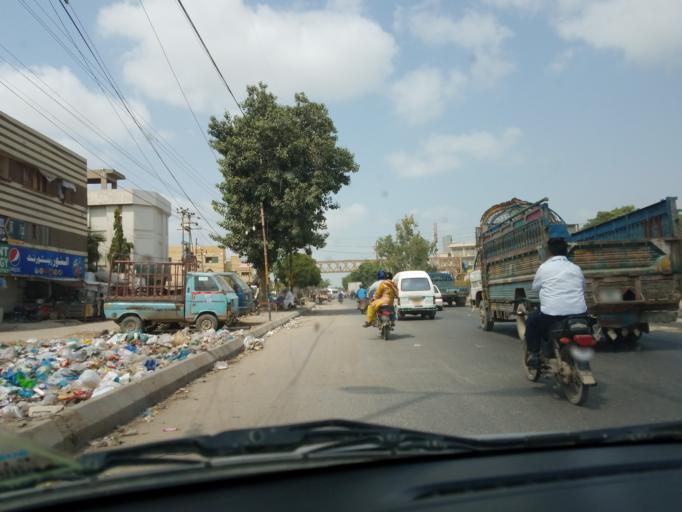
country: PK
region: Sindh
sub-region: Karachi District
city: Karachi
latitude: 24.9488
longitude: 67.0818
